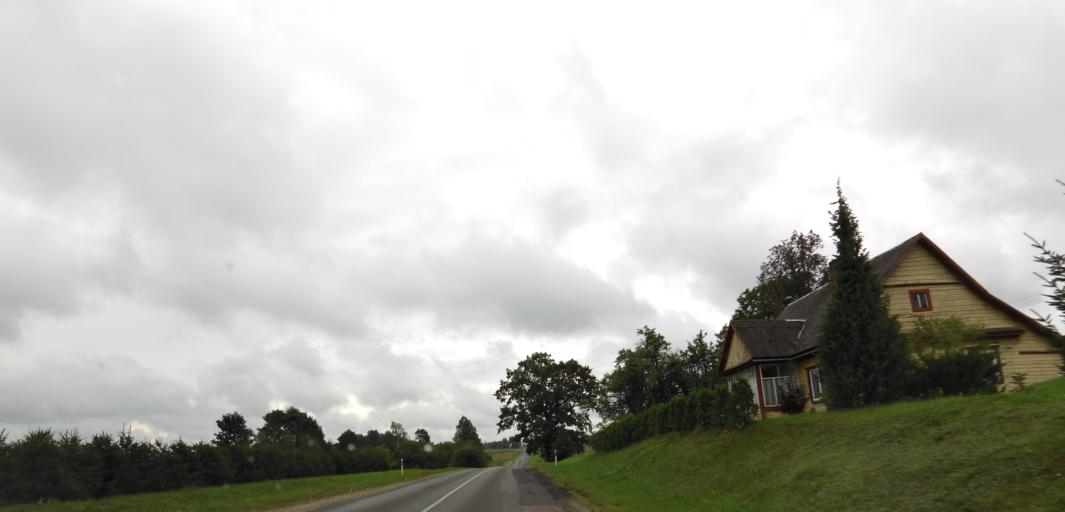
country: LT
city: Moletai
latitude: 55.2910
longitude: 25.3459
